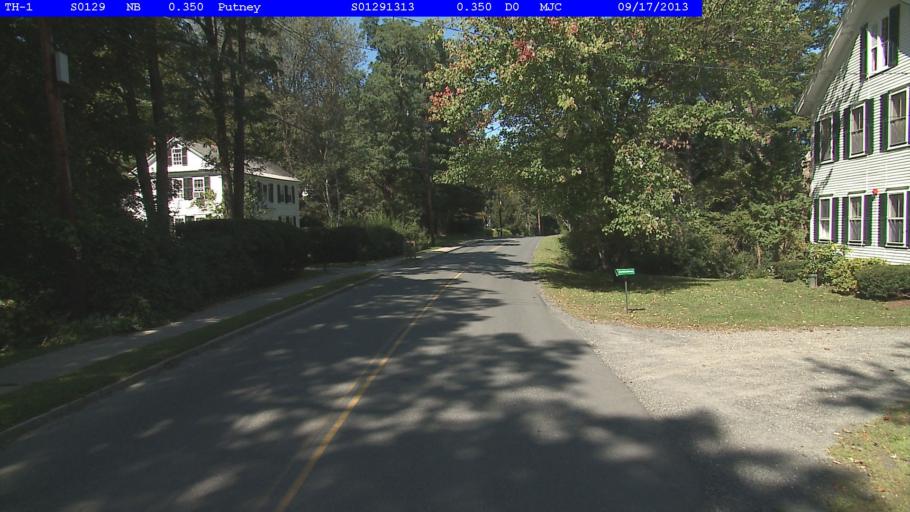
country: US
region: New Hampshire
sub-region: Cheshire County
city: Westmoreland
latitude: 42.9780
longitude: -72.5272
